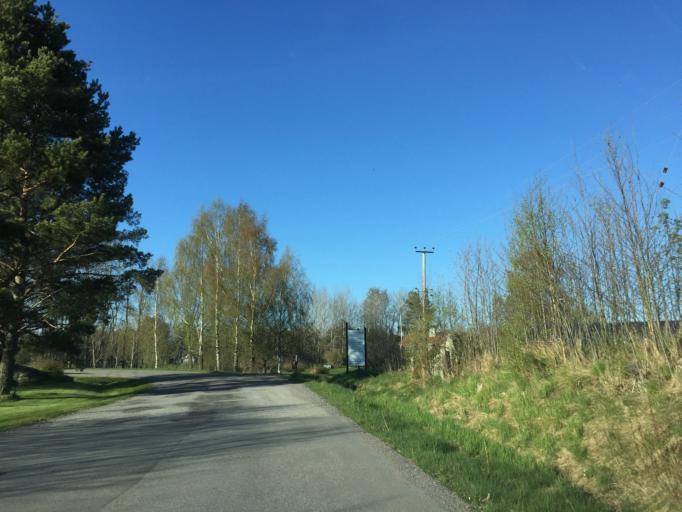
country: SE
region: OErebro
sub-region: Orebro Kommun
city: Odensbacken
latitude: 59.2164
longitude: 15.5611
